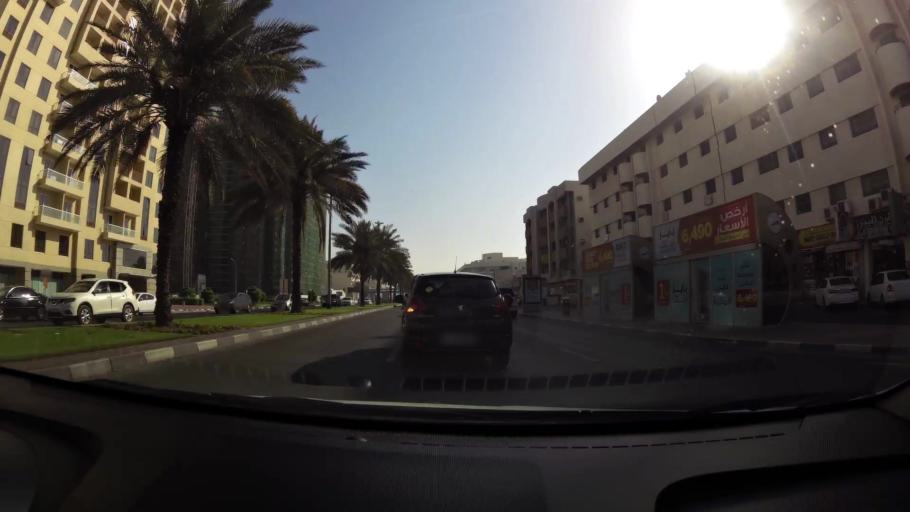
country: AE
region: Ash Shariqah
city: Sharjah
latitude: 25.2713
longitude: 55.3804
